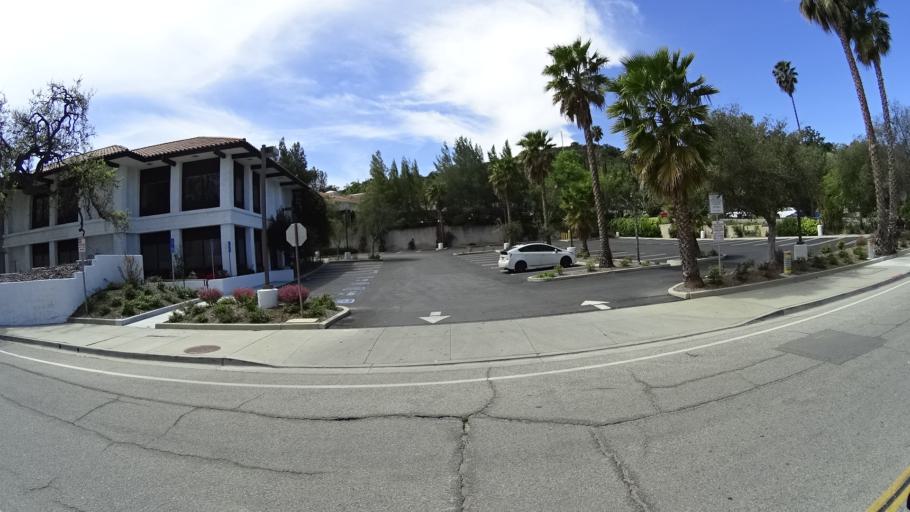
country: US
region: California
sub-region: Ventura County
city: Thousand Oaks
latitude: 34.1658
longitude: -118.8393
